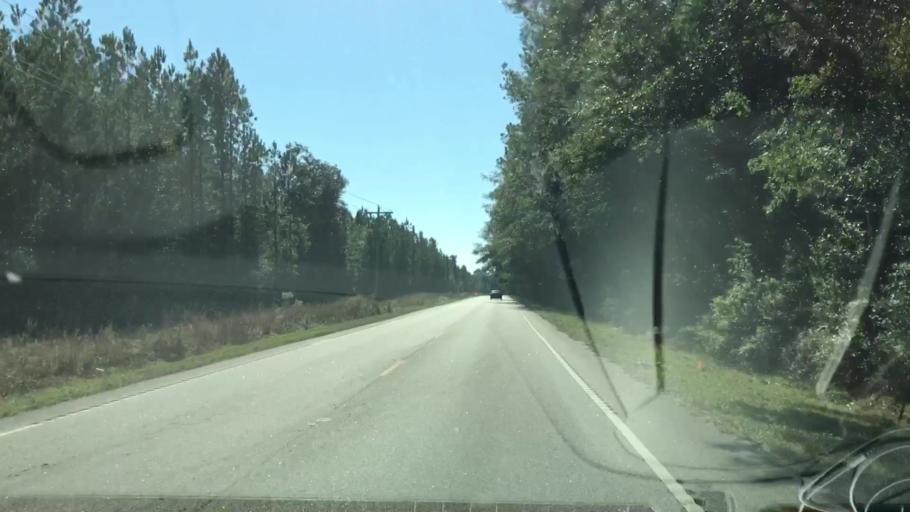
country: US
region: South Carolina
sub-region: Jasper County
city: Ridgeland
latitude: 32.5031
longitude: -80.8865
